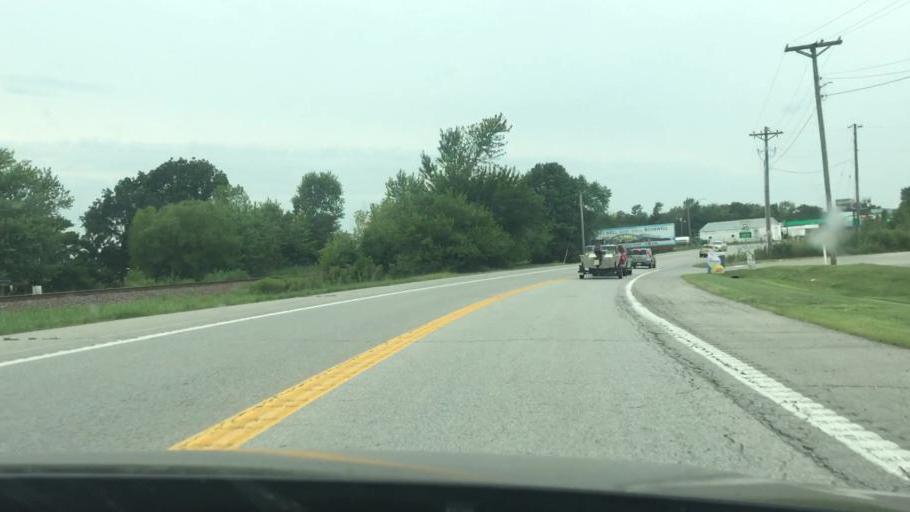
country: US
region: Missouri
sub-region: Pettis County
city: Sedalia
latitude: 38.6973
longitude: -93.1802
